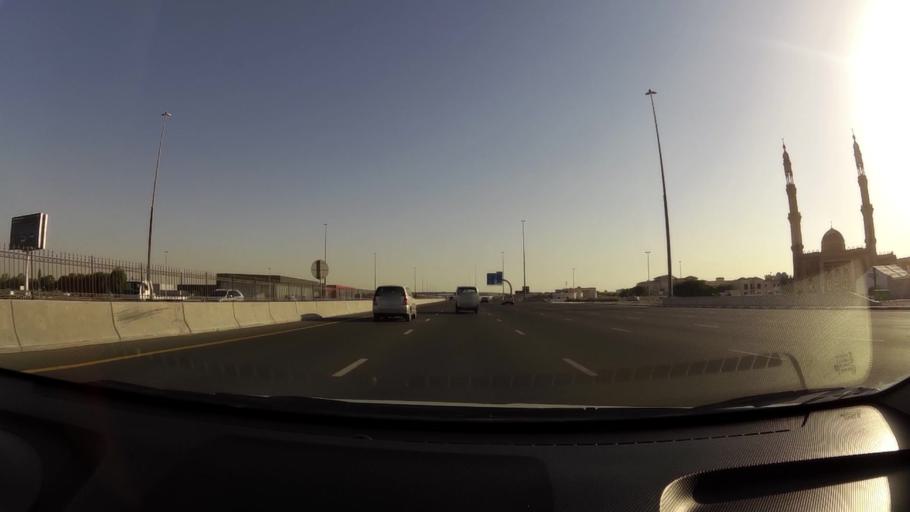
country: AE
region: Ash Shariqah
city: Sharjah
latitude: 25.3441
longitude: 55.4721
